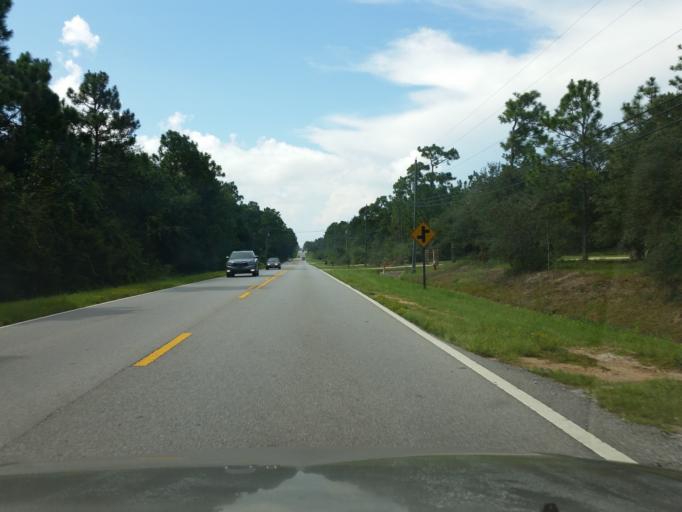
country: US
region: Florida
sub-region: Escambia County
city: Myrtle Grove
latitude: 30.3567
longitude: -87.4028
